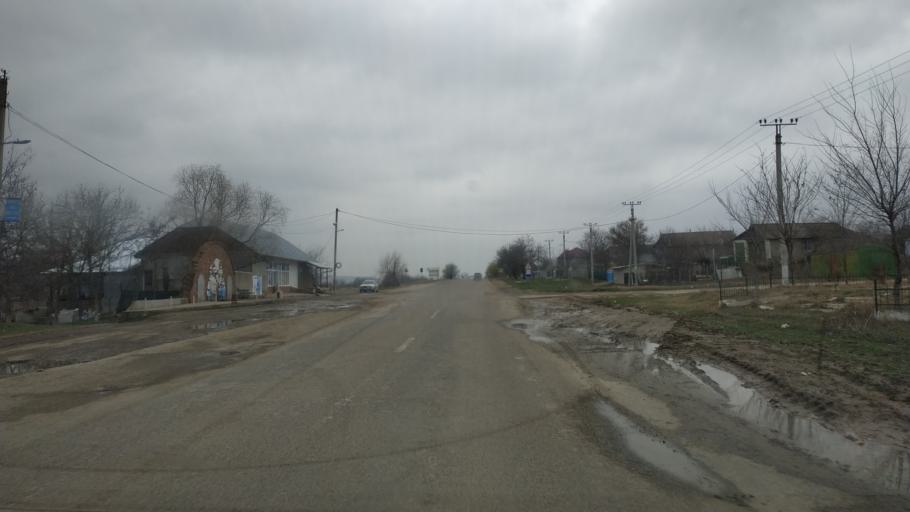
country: MD
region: Cantemir
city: Cantemir
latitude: 46.3215
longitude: 28.2796
